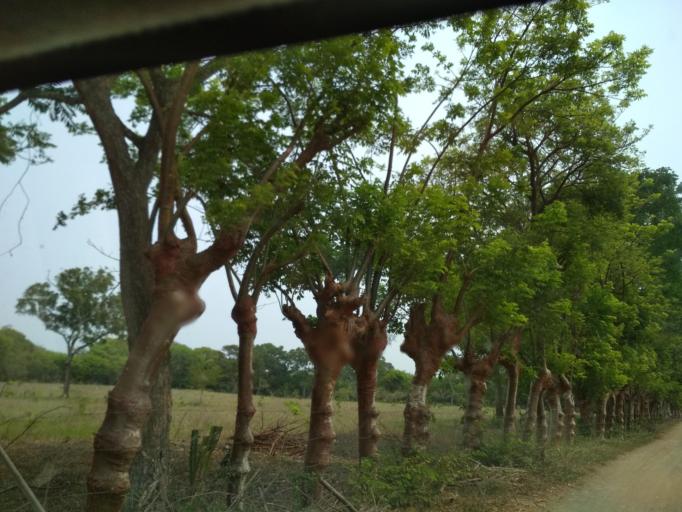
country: MX
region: Veracruz
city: El Tejar
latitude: 19.0658
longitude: -96.1537
